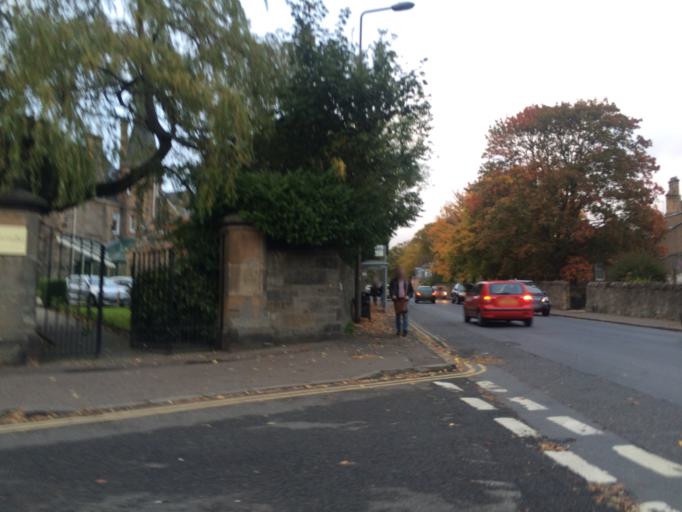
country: GB
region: Scotland
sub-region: Edinburgh
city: Edinburgh
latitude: 55.9289
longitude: -3.1886
